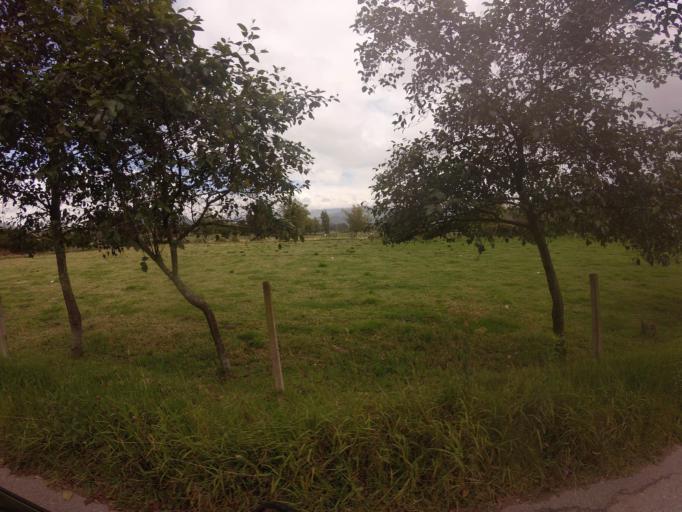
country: CO
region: Boyaca
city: Nobsa
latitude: 5.7816
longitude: -72.9726
